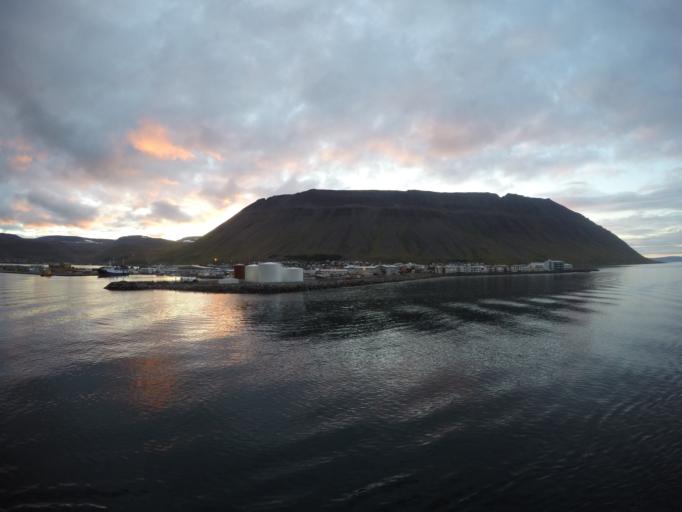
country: IS
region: Westfjords
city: Isafjoerdur
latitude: 66.0678
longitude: -23.1120
